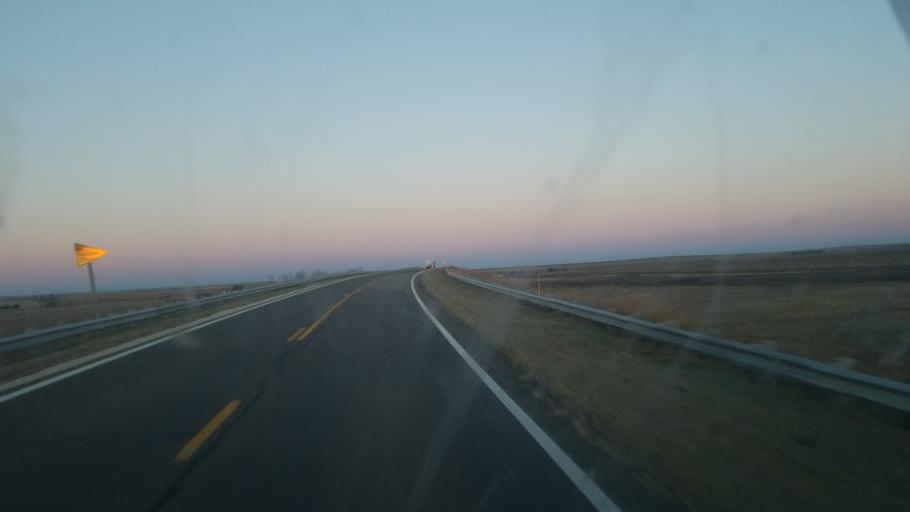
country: US
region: Kansas
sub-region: Wallace County
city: Sharon Springs
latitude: 38.9053
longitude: -101.6145
